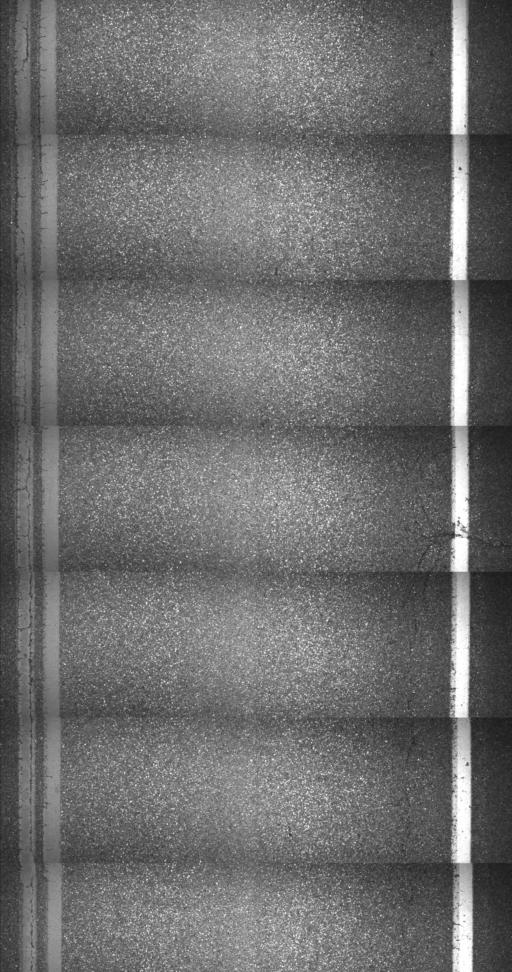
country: US
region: New York
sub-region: Essex County
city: Ticonderoga
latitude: 43.9133
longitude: -73.3118
